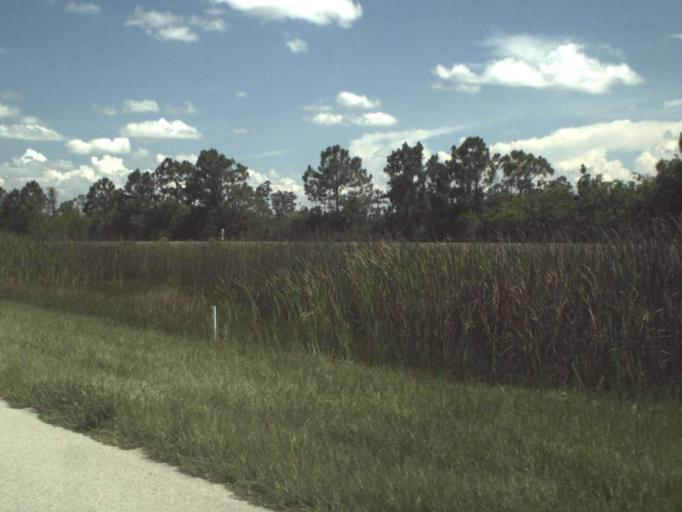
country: US
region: Florida
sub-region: Martin County
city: Indiantown
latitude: 26.9280
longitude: -80.3293
